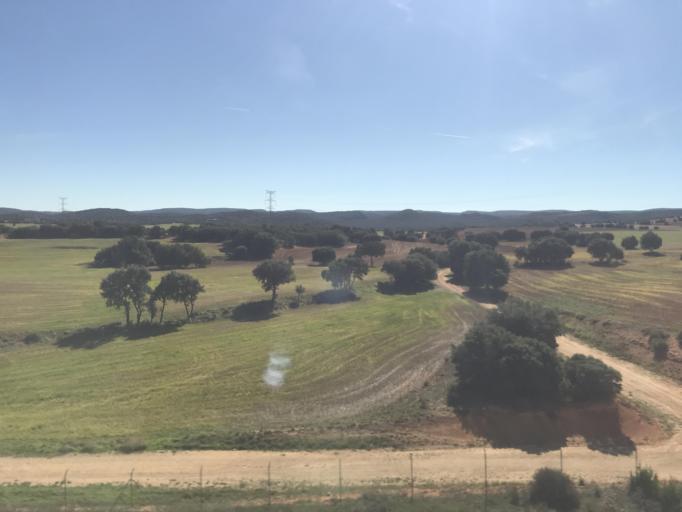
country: ES
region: Aragon
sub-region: Provincia de Zaragoza
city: Alconchel de Ariza
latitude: 41.1985
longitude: -2.1574
